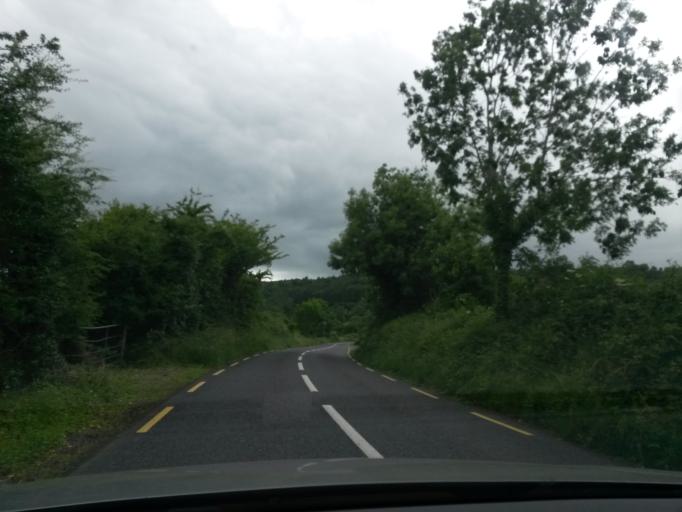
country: IE
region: Connaught
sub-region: Sligo
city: Sligo
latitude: 54.2624
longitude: -8.3212
